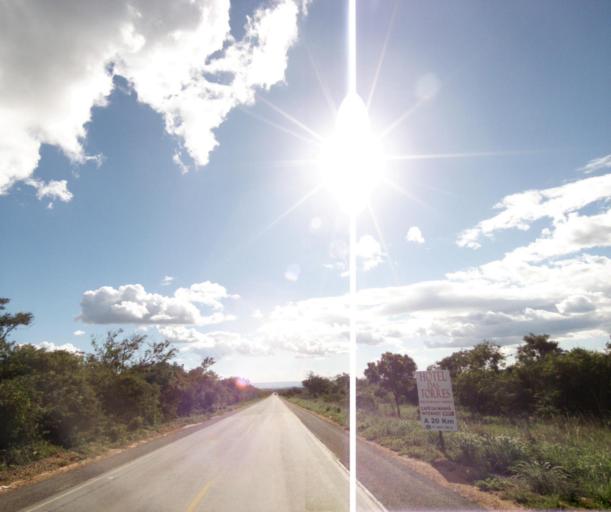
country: BR
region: Bahia
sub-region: Caetite
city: Caetite
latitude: -14.1267
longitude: -42.6212
